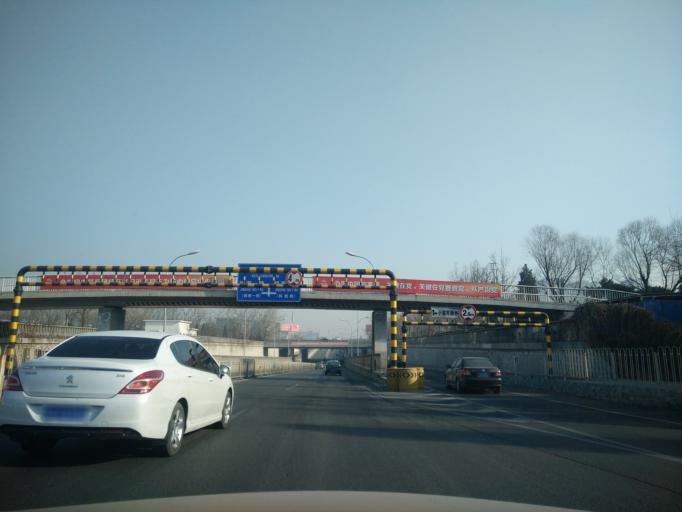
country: CN
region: Beijing
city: Jiugong
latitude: 39.7991
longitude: 116.5194
